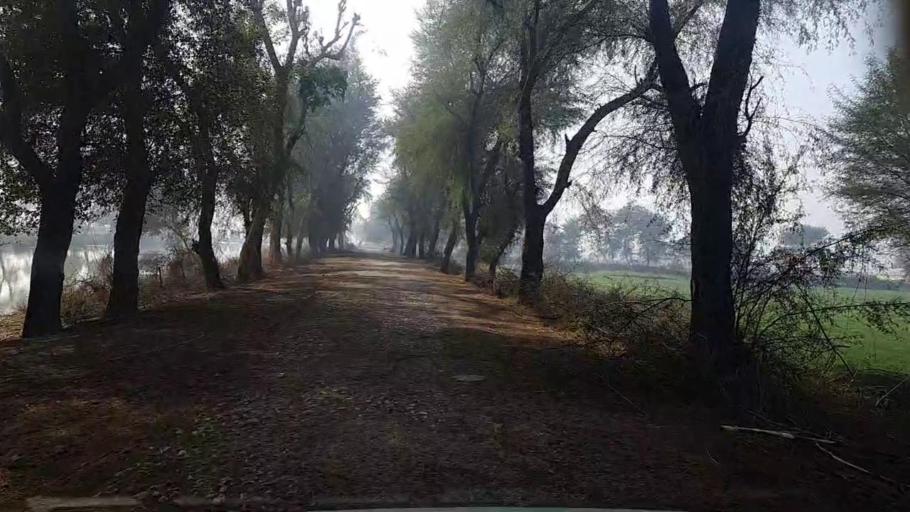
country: PK
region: Sindh
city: Khairpur
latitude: 27.9528
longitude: 69.6526
